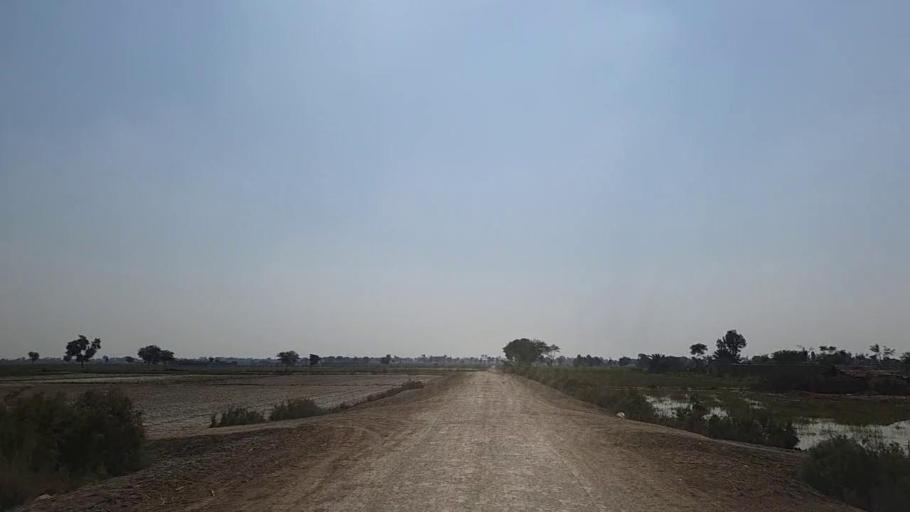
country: PK
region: Sindh
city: Daur
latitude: 26.4554
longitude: 68.2708
